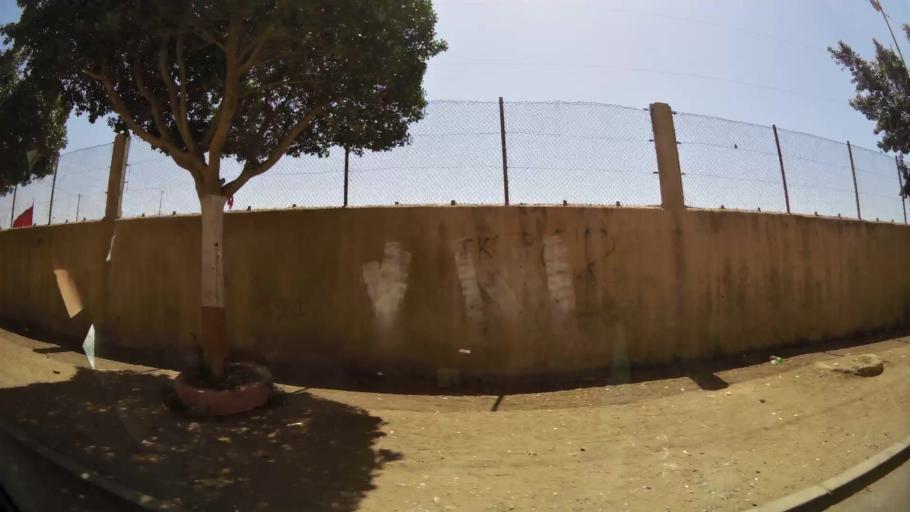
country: MA
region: Souss-Massa-Draa
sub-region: Inezgane-Ait Mellou
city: Inezgane
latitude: 30.3463
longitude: -9.4893
